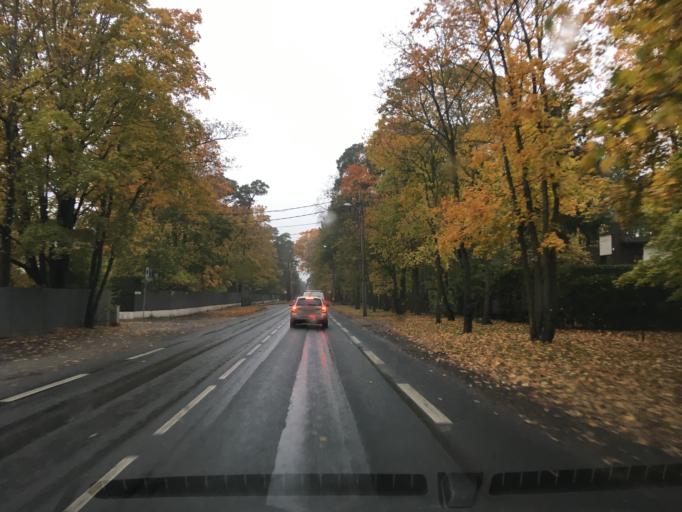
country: EE
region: Harju
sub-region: Tallinna linn
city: Kose
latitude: 59.4582
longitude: 24.8553
